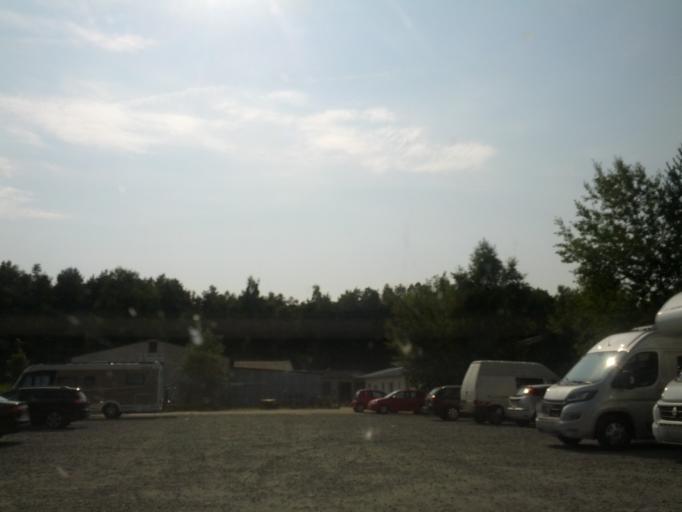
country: DE
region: Mecklenburg-Vorpommern
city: Ostseebad Binz
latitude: 54.4041
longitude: 13.6000
